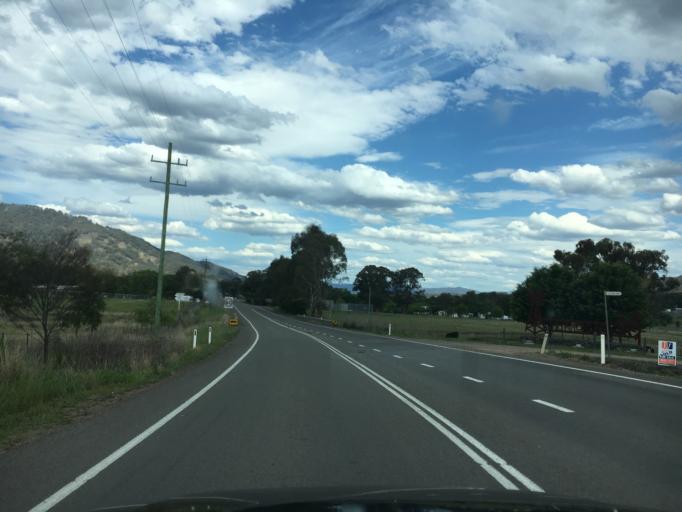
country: AU
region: New South Wales
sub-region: Liverpool Plains
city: Quirindi
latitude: -31.7566
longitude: 150.8184
